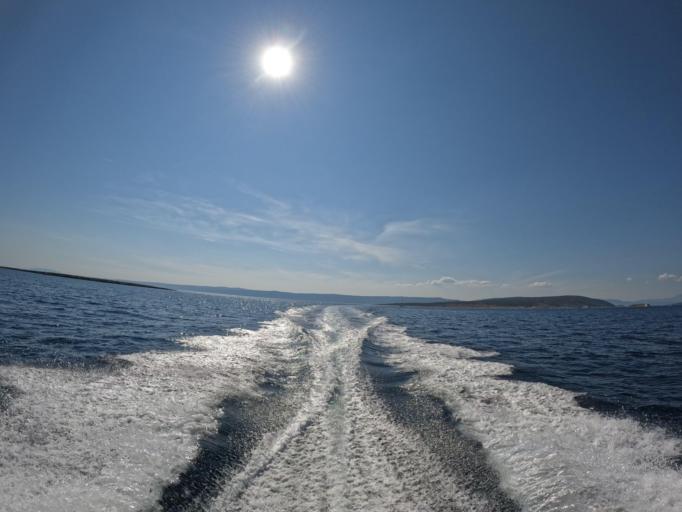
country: HR
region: Primorsko-Goranska
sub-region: Grad Krk
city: Krk
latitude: 44.9544
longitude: 14.5755
